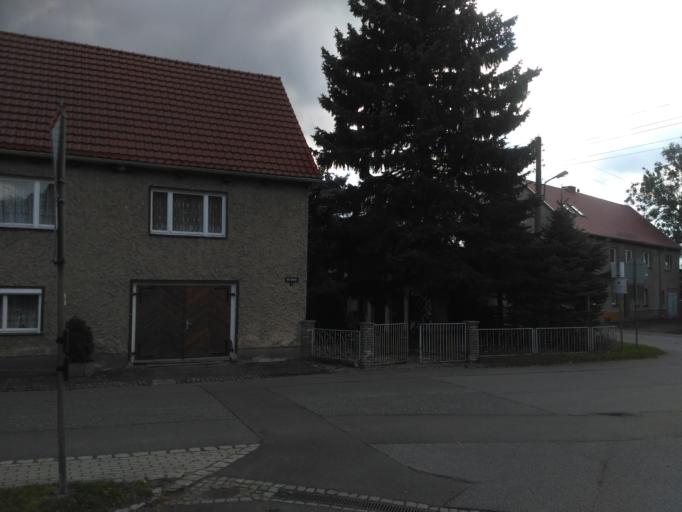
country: DE
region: Saxony
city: Hohnstein
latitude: 51.0077
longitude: 14.0904
